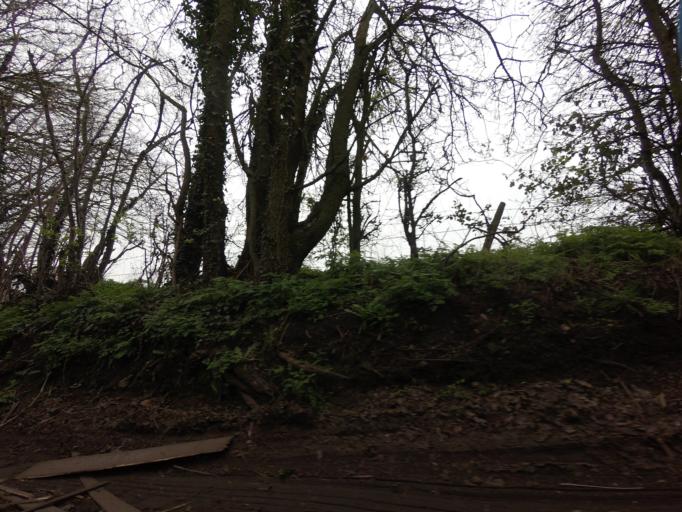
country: GB
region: England
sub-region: Kent
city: Swanley
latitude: 51.3752
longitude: 0.1587
